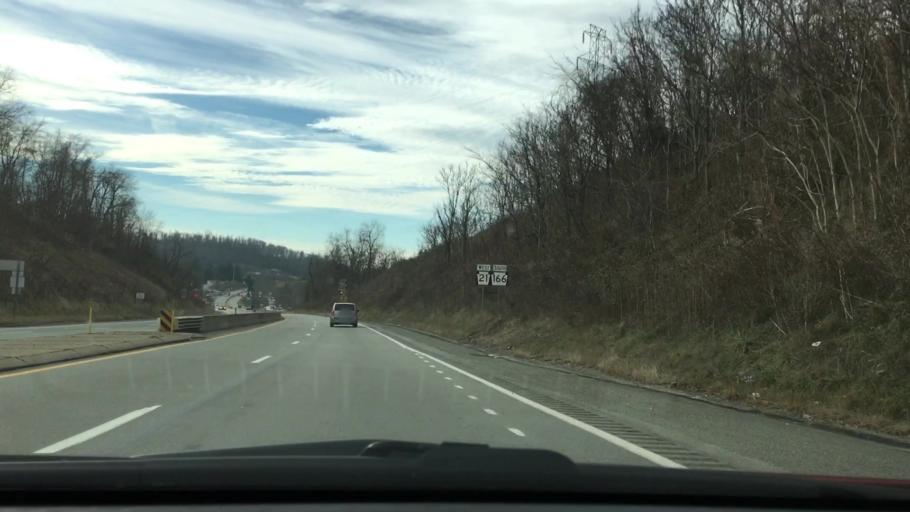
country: US
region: Pennsylvania
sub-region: Fayette County
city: Masontown
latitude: 39.8699
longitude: -79.8910
